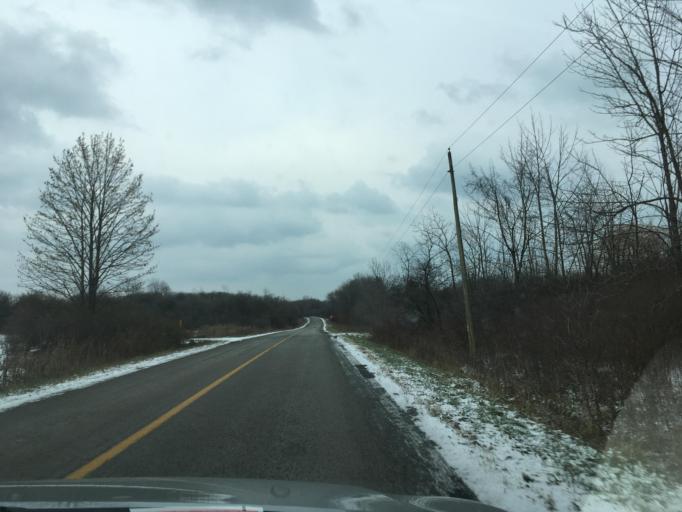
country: CA
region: Ontario
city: Norfolk County
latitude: 42.7903
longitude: -80.1115
